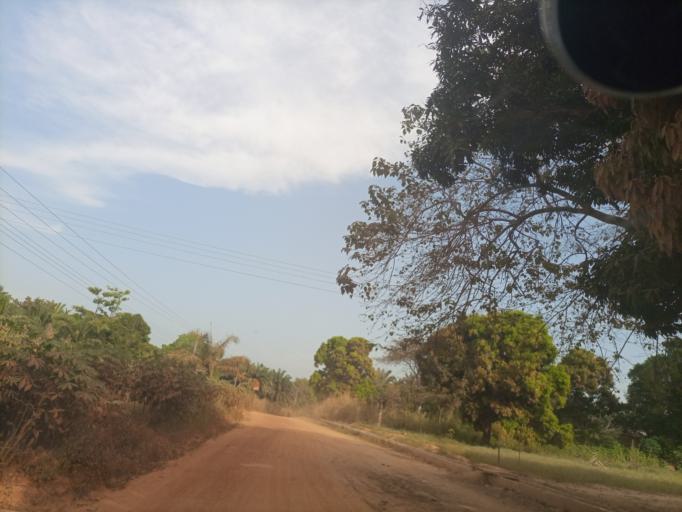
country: NG
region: Enugu
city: Obolo-Eke (1)
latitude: 6.8091
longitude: 7.5529
